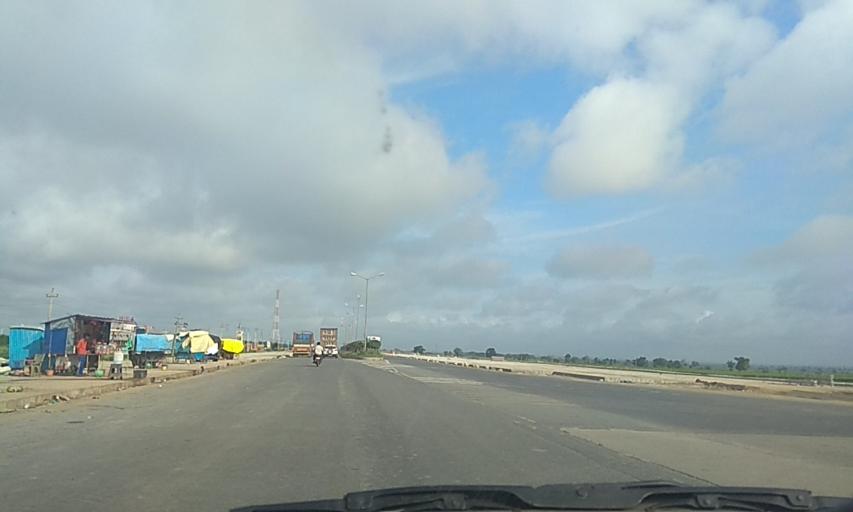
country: IN
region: Karnataka
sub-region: Haveri
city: Savanur
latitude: 14.9104
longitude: 75.2792
